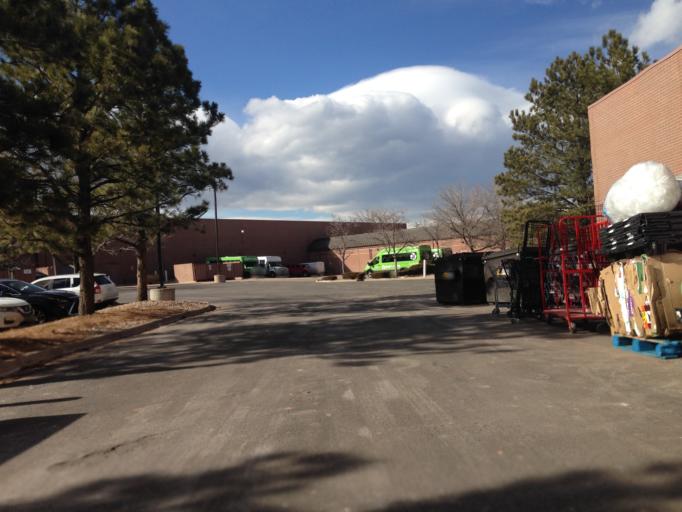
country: US
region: Colorado
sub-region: Boulder County
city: Boulder
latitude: 39.9979
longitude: -105.2349
